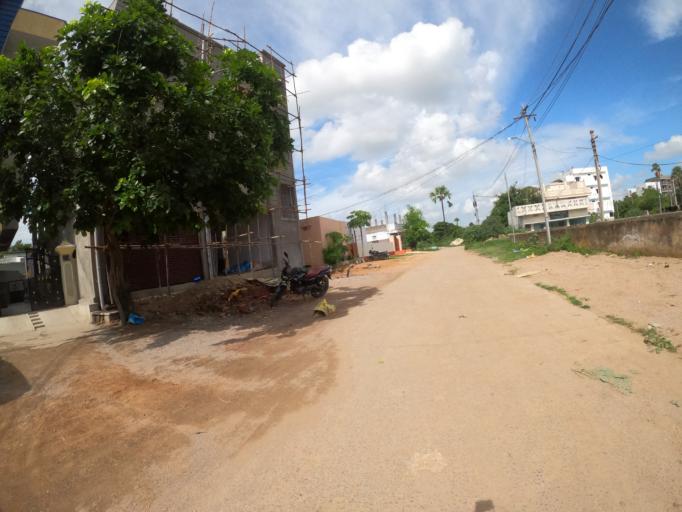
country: IN
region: Telangana
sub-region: Hyderabad
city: Hyderabad
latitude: 17.3517
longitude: 78.3915
